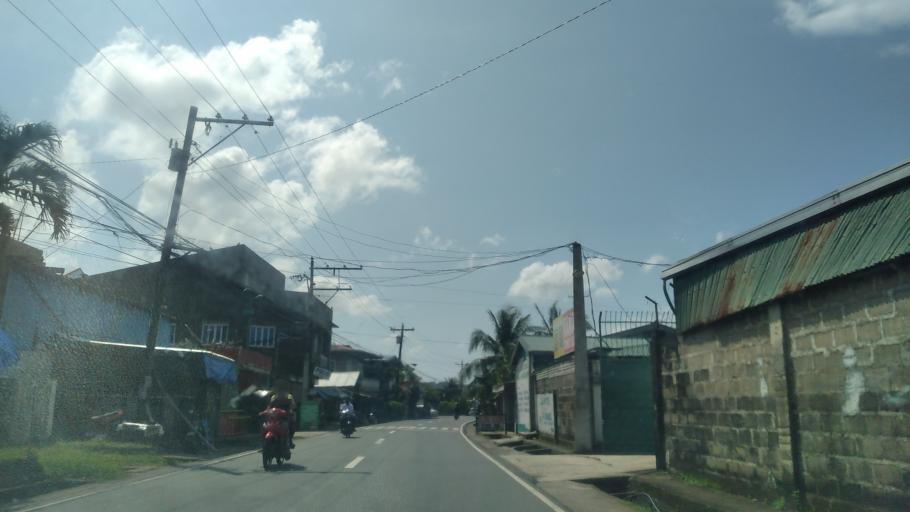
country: PH
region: Calabarzon
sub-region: Province of Quezon
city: Unisan
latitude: 13.8376
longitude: 121.9773
